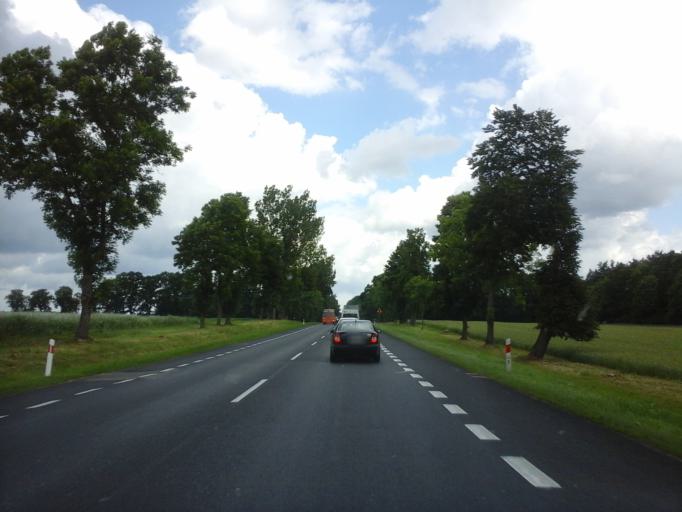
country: PL
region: West Pomeranian Voivodeship
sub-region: Powiat bialogardzki
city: Bialogard
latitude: 54.0959
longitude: 15.9930
